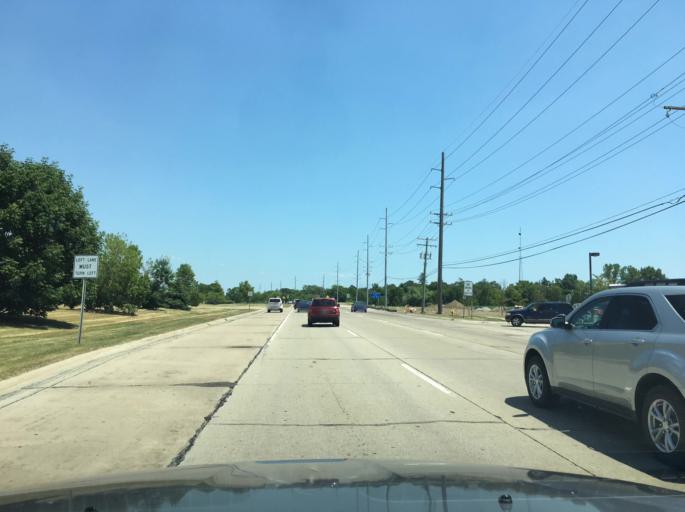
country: US
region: Michigan
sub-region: Macomb County
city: Mount Clemens
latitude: 42.6286
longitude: -82.8940
